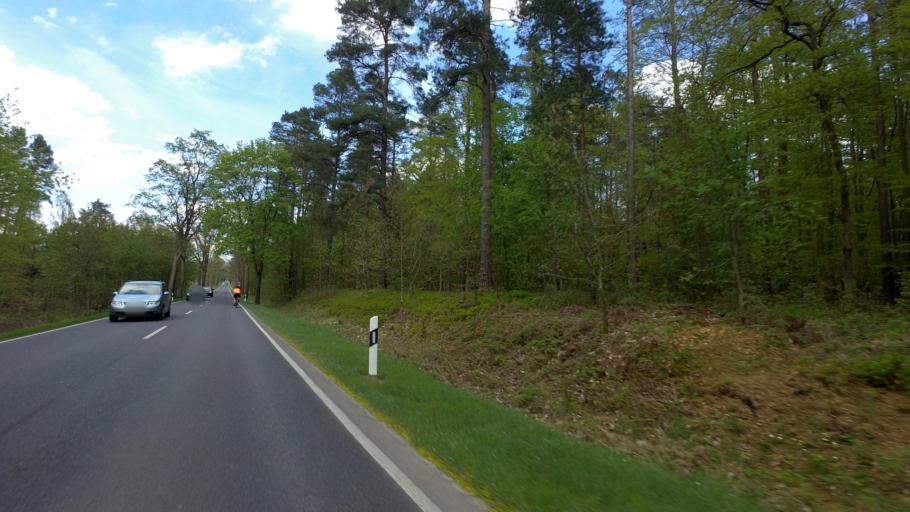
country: DE
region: Brandenburg
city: Marienwerder
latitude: 52.9772
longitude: 13.5805
